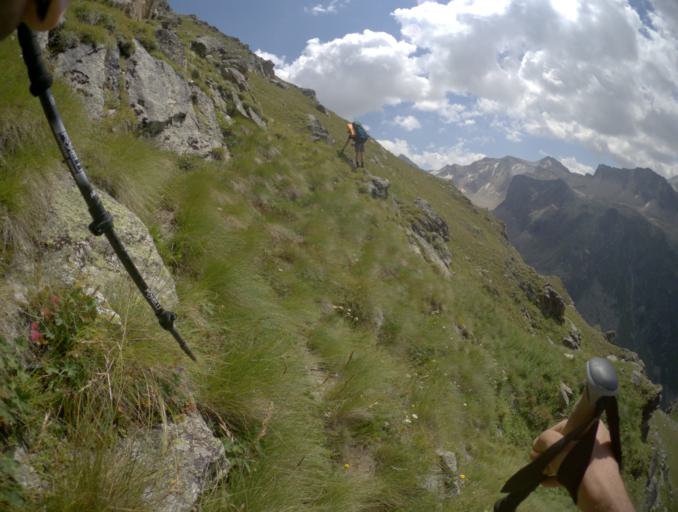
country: RU
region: Karachayevo-Cherkesiya
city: Uchkulan
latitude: 43.2966
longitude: 42.0695
